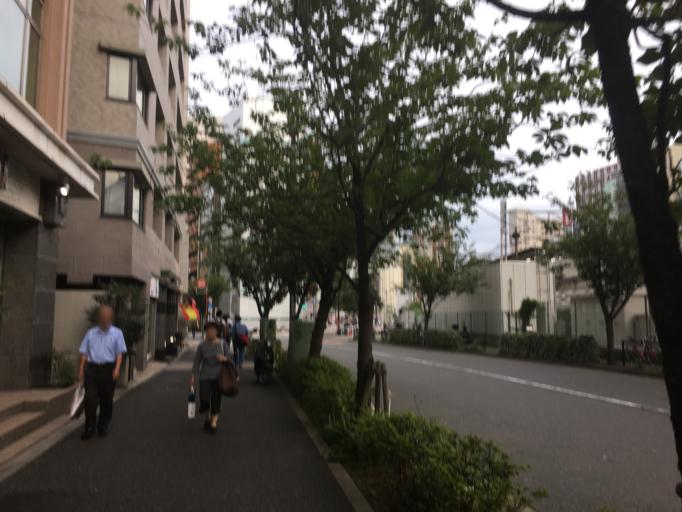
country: JP
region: Tokyo
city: Tokyo
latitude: 35.6279
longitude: 139.7221
